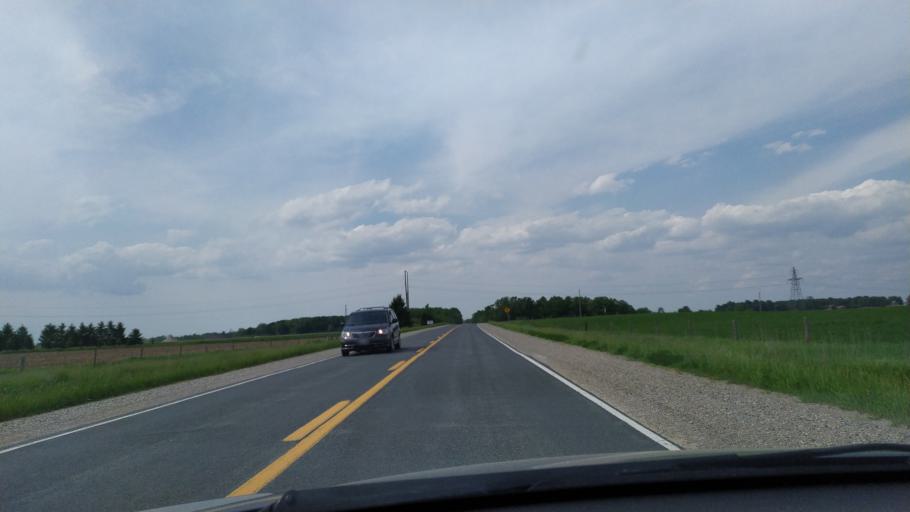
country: CA
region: Ontario
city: Ingersoll
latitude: 43.0360
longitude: -80.9759
